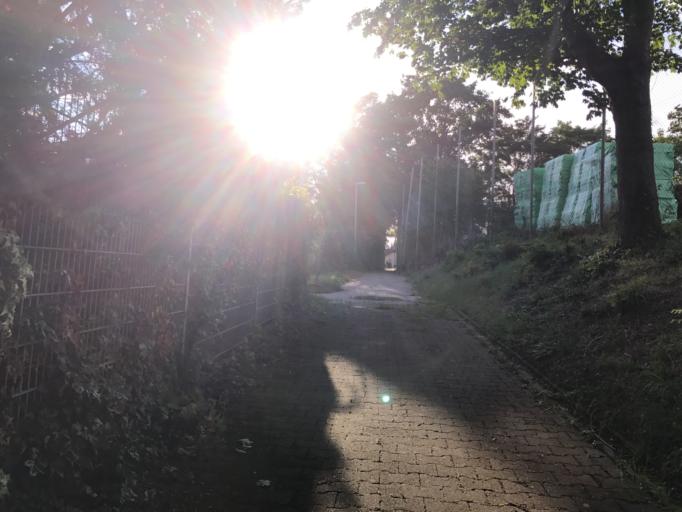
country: DE
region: Rheinland-Pfalz
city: Mainz
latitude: 50.0022
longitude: 8.2249
